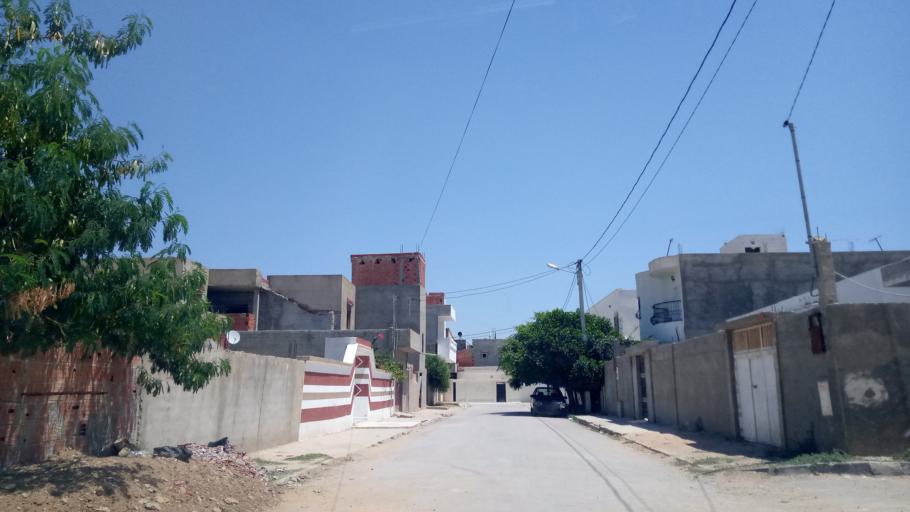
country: TN
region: Al Qayrawan
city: Sbikha
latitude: 36.1180
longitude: 10.0901
